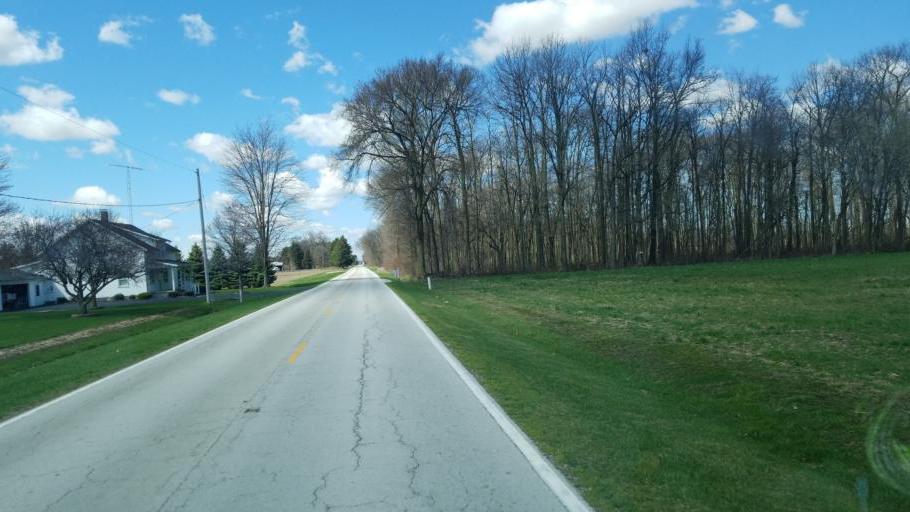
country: US
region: Ohio
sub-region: Sandusky County
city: Green Springs
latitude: 41.2567
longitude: -83.0950
